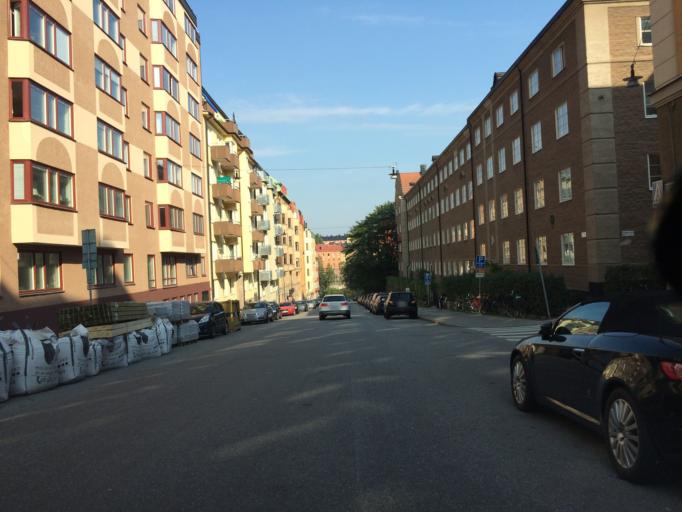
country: SE
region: Stockholm
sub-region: Stockholms Kommun
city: Stockholm
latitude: 59.3345
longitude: 18.0358
